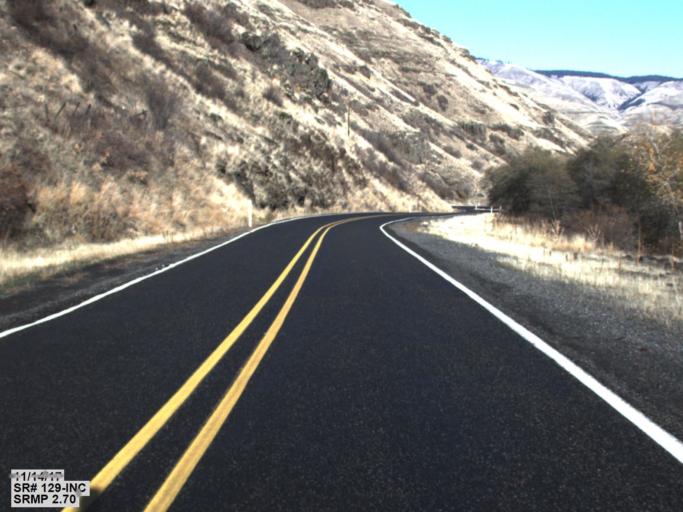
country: US
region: Washington
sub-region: Asotin County
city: Asotin
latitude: 46.0197
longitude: -117.2636
